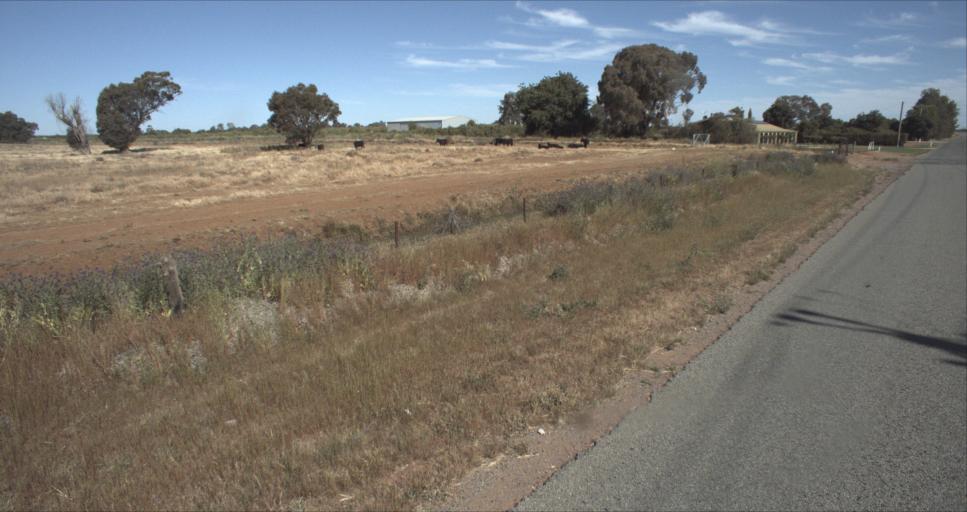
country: AU
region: New South Wales
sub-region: Leeton
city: Leeton
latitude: -34.5633
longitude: 146.3832
